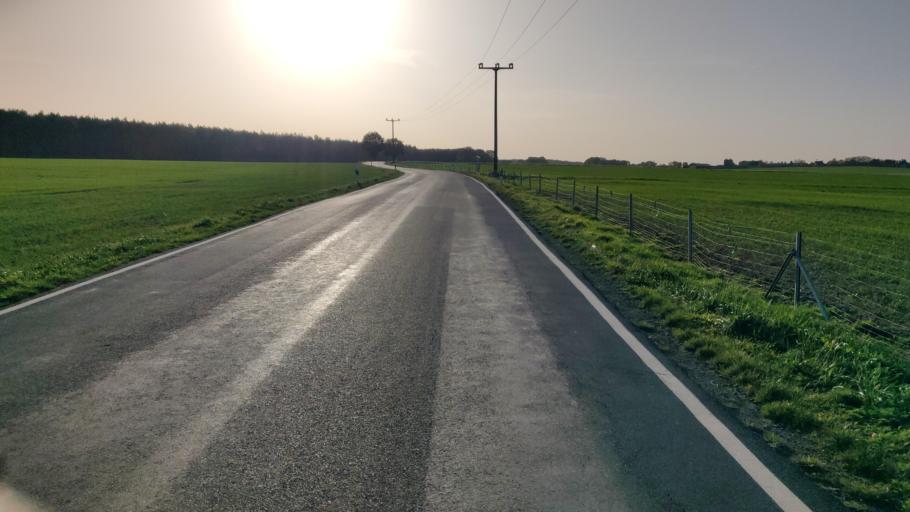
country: DE
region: Saxony
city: Lampertswalde
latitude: 51.3483
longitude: 13.6747
